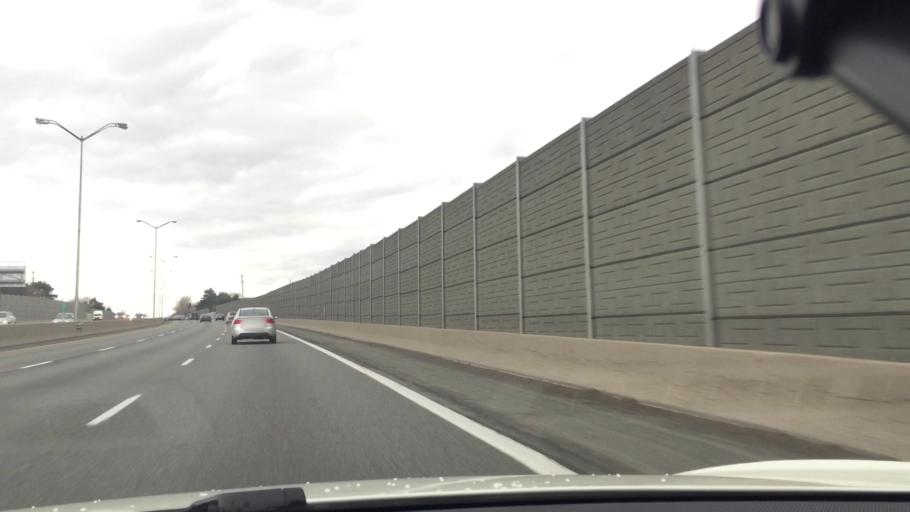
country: CA
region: Ontario
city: Oshawa
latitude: 43.8869
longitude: -78.8332
